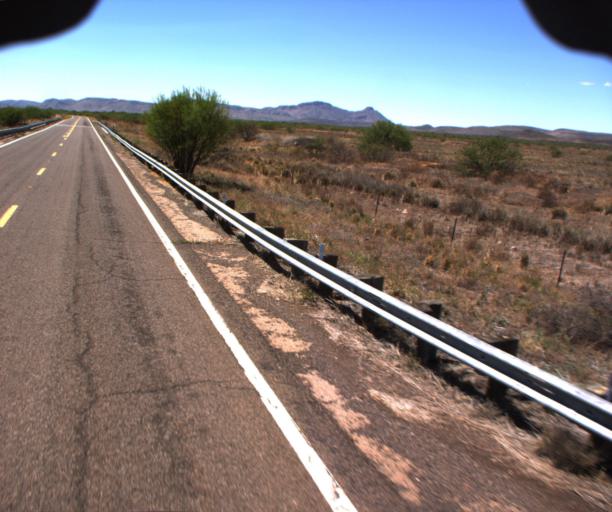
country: US
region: Arizona
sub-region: Cochise County
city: Douglas
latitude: 31.5185
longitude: -109.3061
